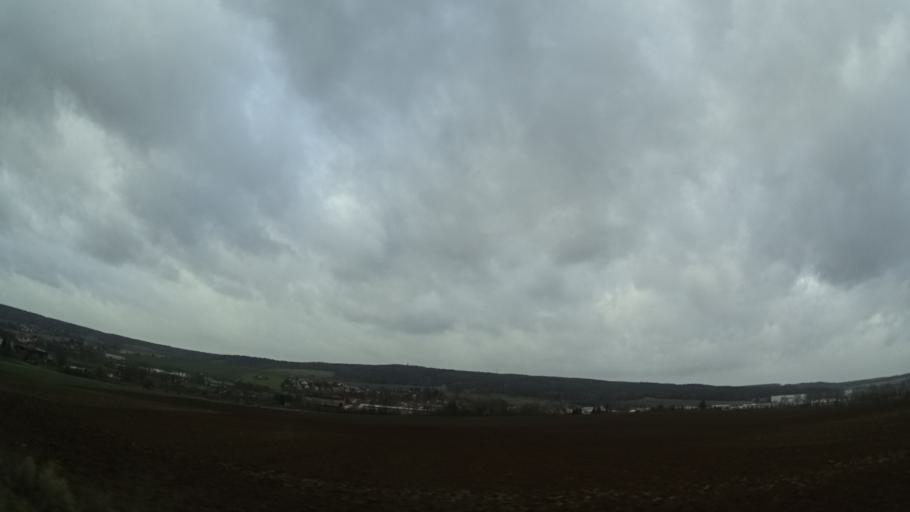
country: DE
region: Thuringia
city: Neustadt (Orla)
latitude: 50.7321
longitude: 11.7681
